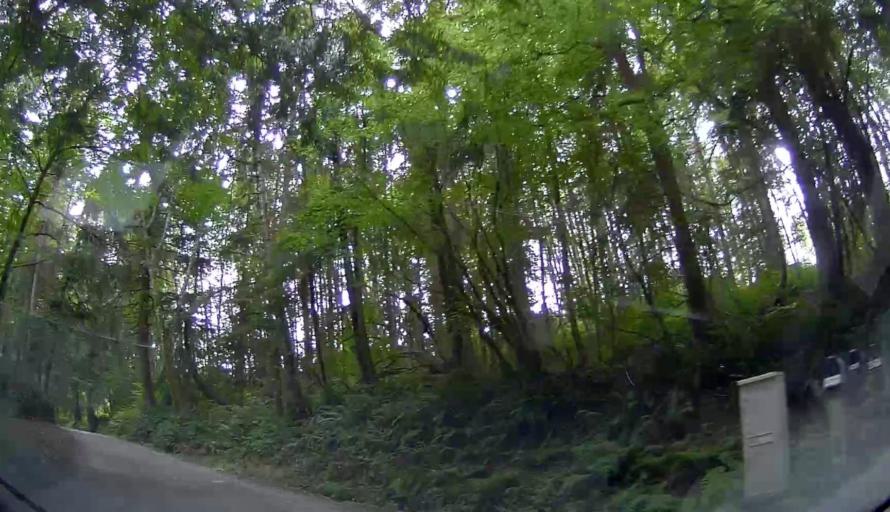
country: US
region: Washington
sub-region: Whatcom County
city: Sudden Valley
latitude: 48.5943
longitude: -122.3958
